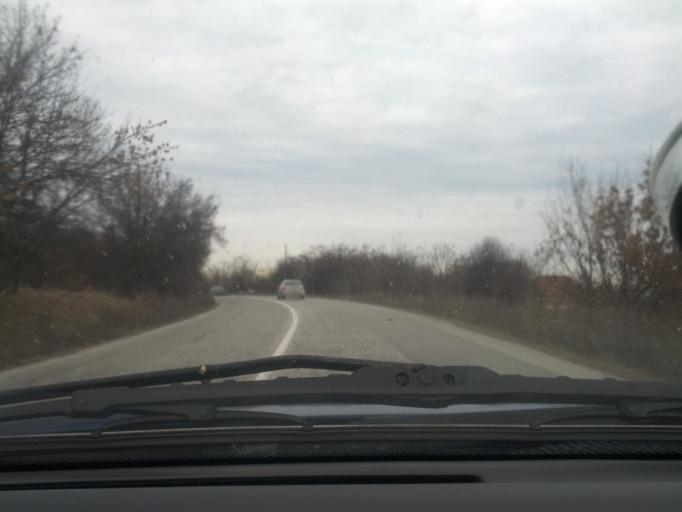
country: BG
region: Vratsa
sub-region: Obshtina Borovan
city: Borovan
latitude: 43.3722
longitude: 23.7072
